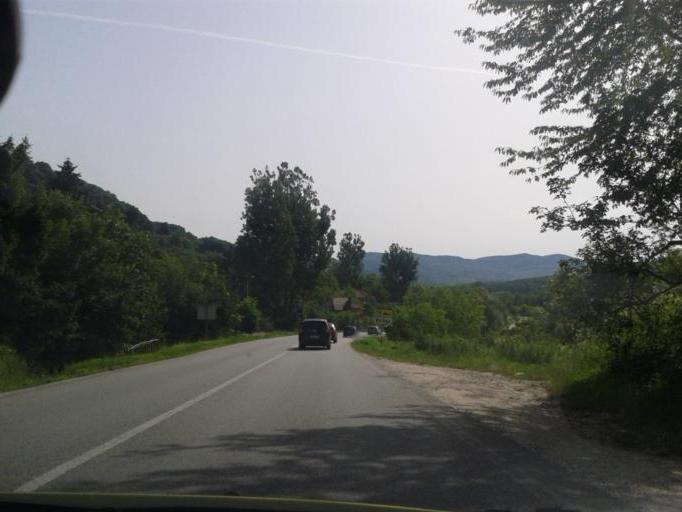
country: RO
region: Valcea
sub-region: Comuna Pietrari
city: Pietrari
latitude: 45.1088
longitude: 24.1409
